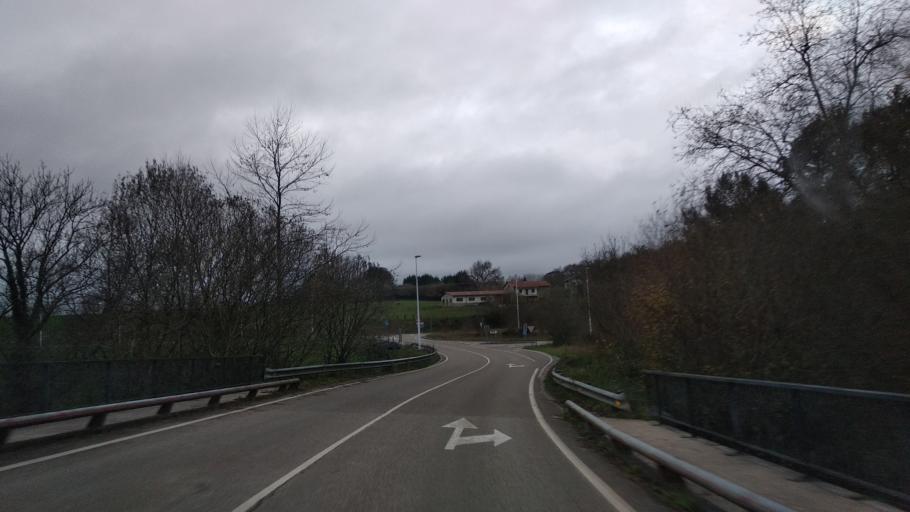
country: ES
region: Cantabria
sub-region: Provincia de Cantabria
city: Entrambasaguas
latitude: 43.4181
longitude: -3.7067
